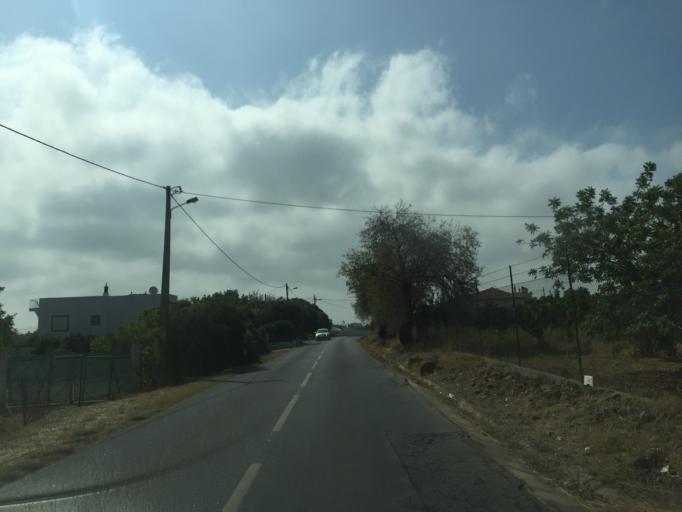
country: PT
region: Faro
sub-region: Olhao
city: Olhao
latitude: 37.0775
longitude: -7.8902
